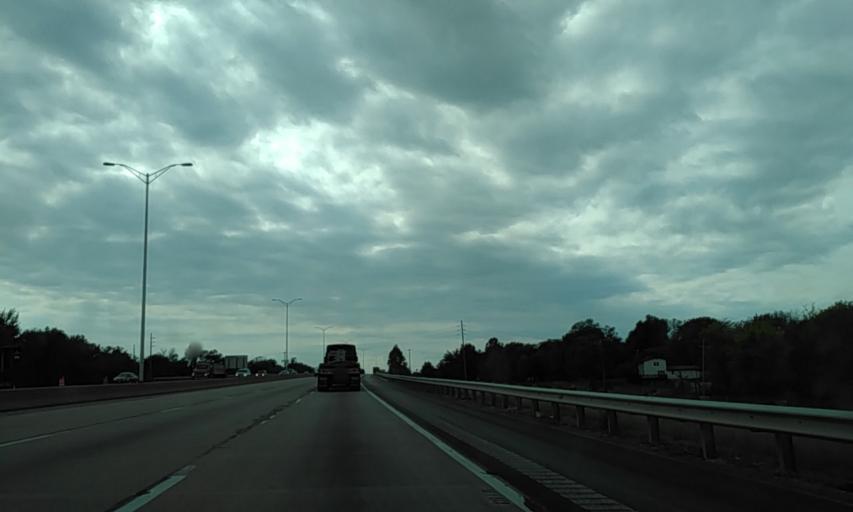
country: US
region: Illinois
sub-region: Saint Clair County
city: Centreville
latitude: 38.5584
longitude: -90.1440
